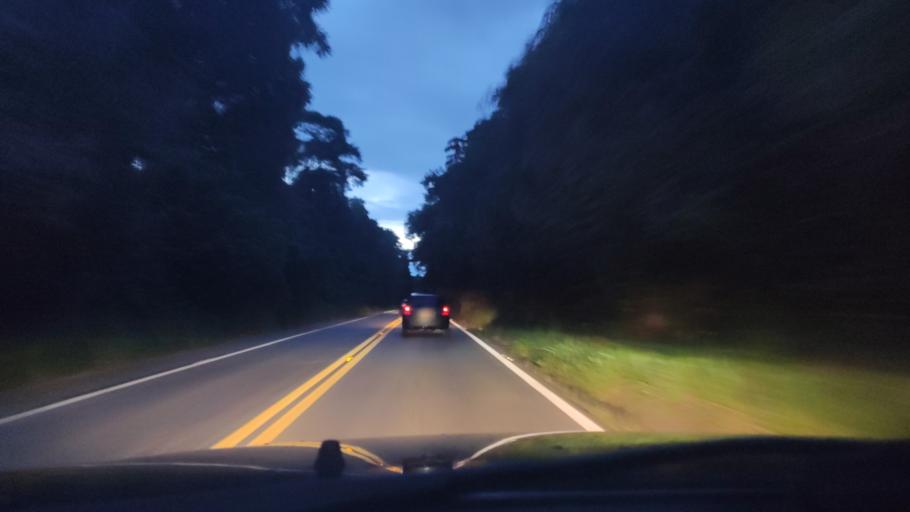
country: BR
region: Sao Paulo
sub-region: Socorro
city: Socorro
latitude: -22.5630
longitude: -46.5453
